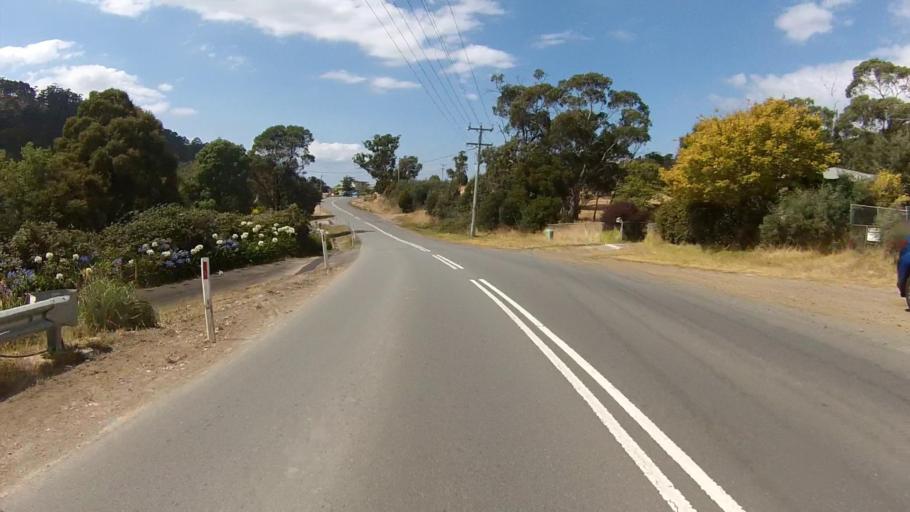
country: AU
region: Tasmania
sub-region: Clarence
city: Cambridge
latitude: -42.8388
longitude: 147.4270
